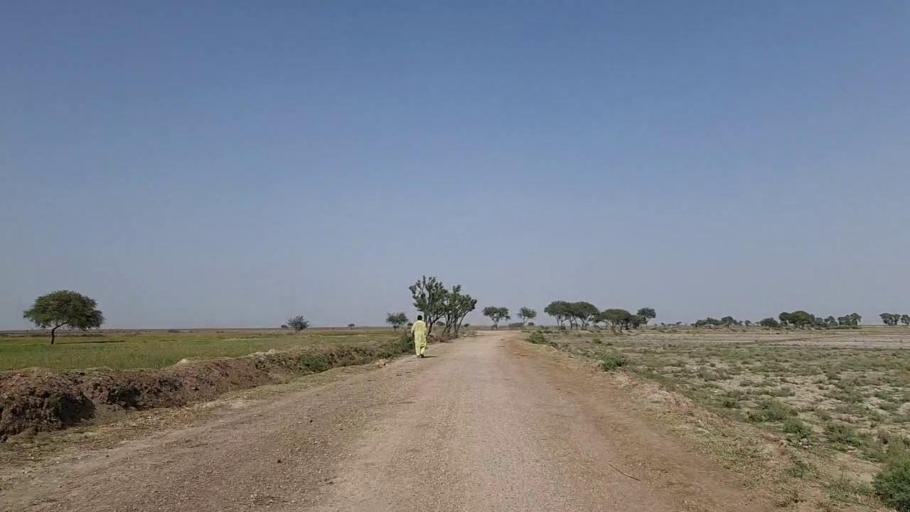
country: PK
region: Sindh
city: Jati
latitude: 24.3483
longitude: 68.3085
